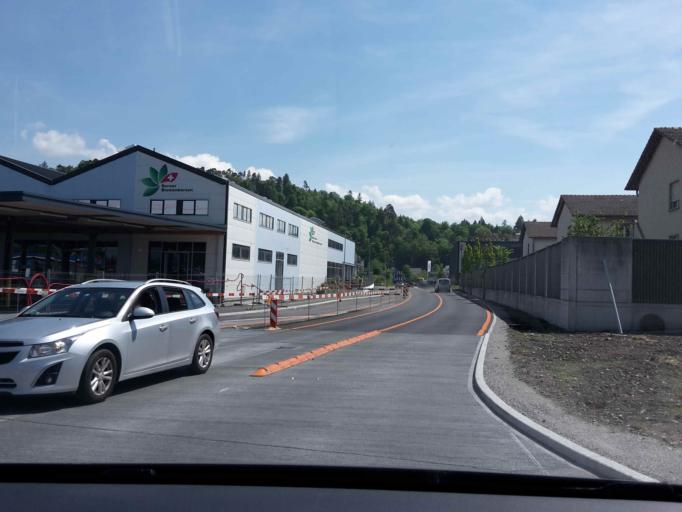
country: CH
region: Bern
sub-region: Thun District
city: Heimberg
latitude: 46.7803
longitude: 7.6047
